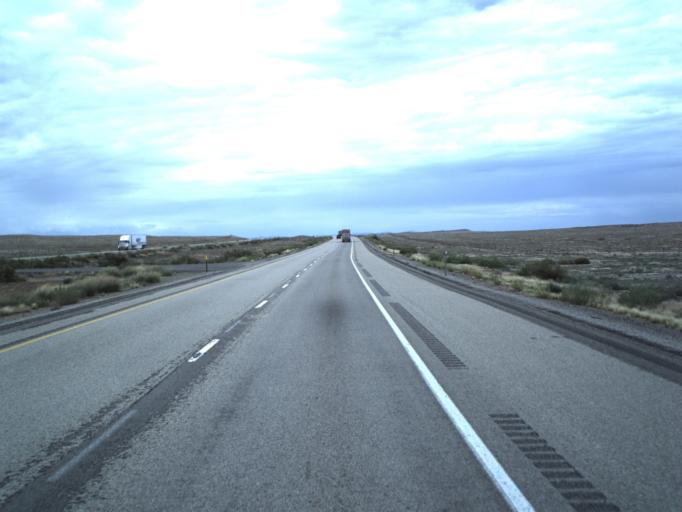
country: US
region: Utah
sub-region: Grand County
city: Moab
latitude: 38.9972
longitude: -109.3248
